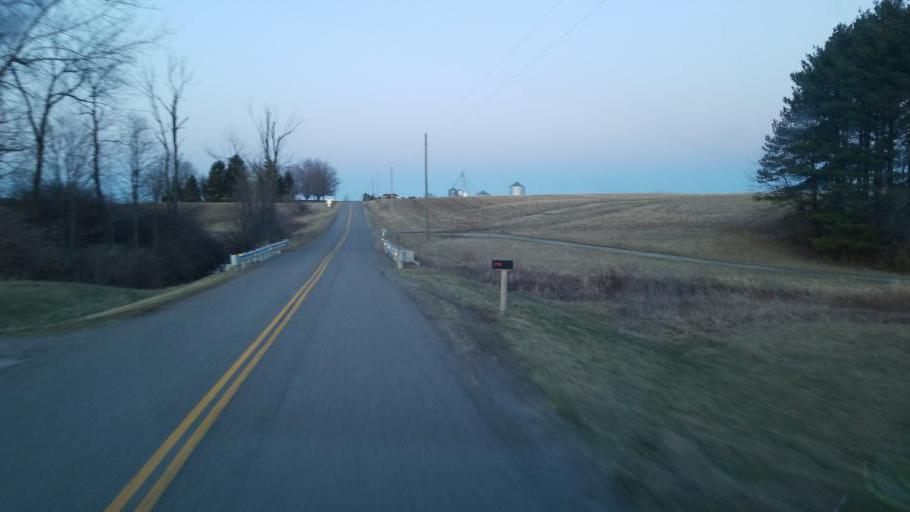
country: US
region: Ohio
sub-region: Champaign County
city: North Lewisburg
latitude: 40.2351
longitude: -83.6205
